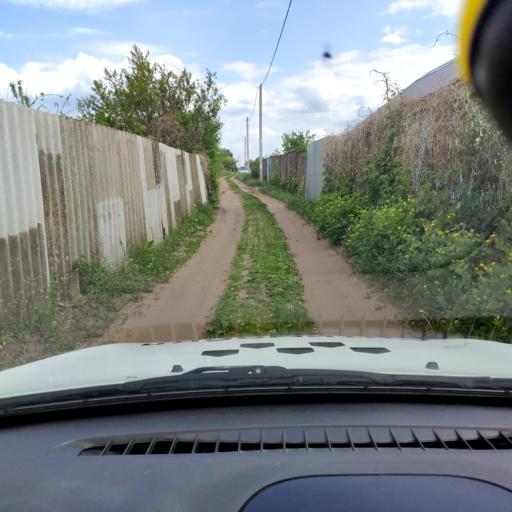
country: RU
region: Samara
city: Zhigulevsk
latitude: 53.5299
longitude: 49.5596
